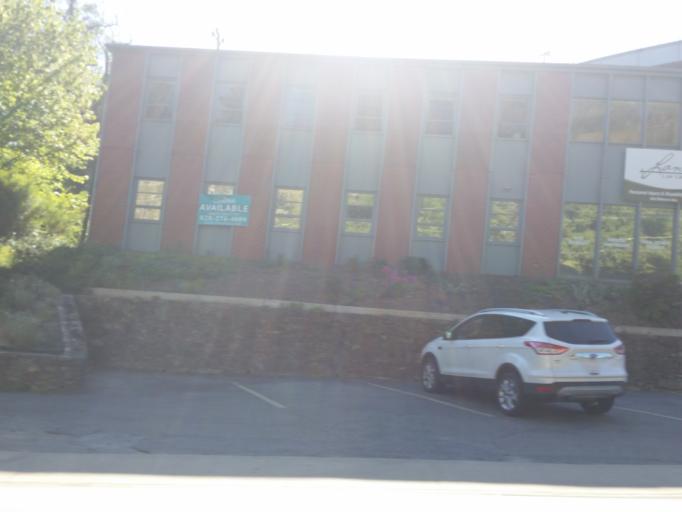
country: US
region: North Carolina
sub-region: Buncombe County
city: Asheville
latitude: 35.5755
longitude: -82.5471
